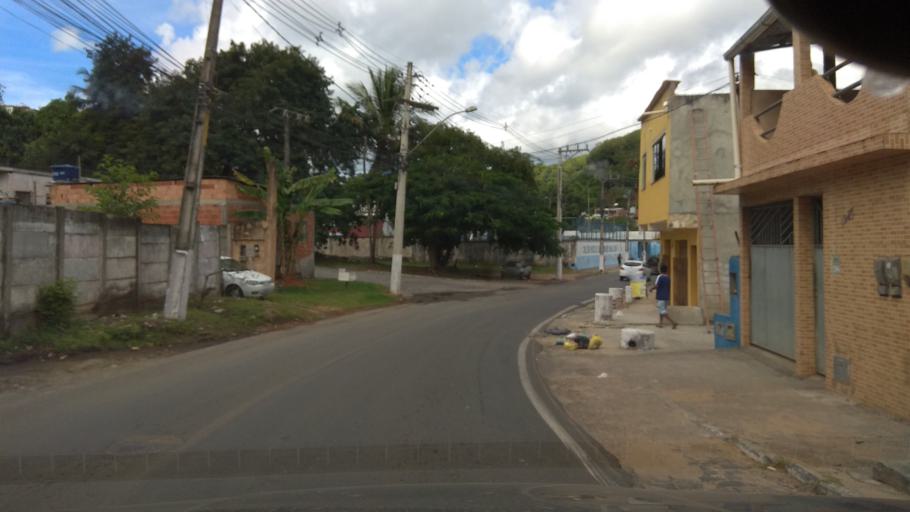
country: BR
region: Bahia
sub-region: Ilheus
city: Ilheus
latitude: -14.7877
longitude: -39.0604
